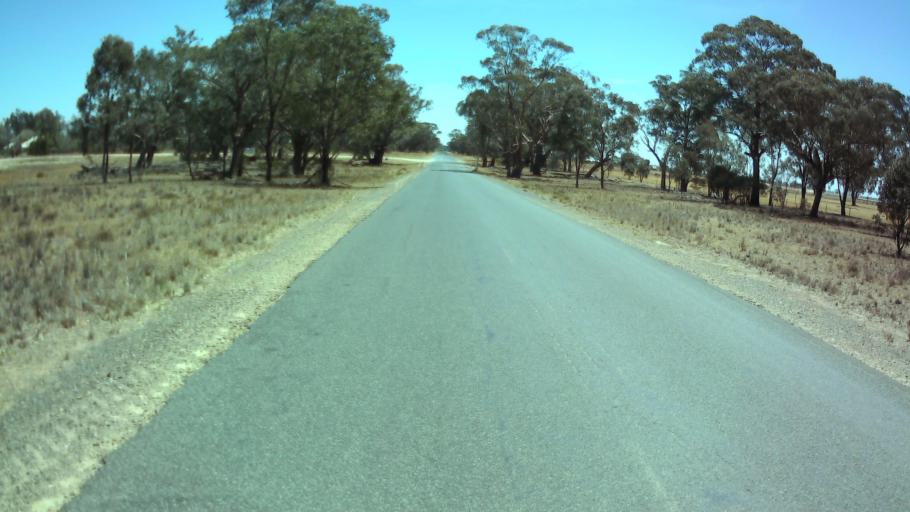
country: AU
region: New South Wales
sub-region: Weddin
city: Grenfell
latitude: -34.0128
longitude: 147.8169
